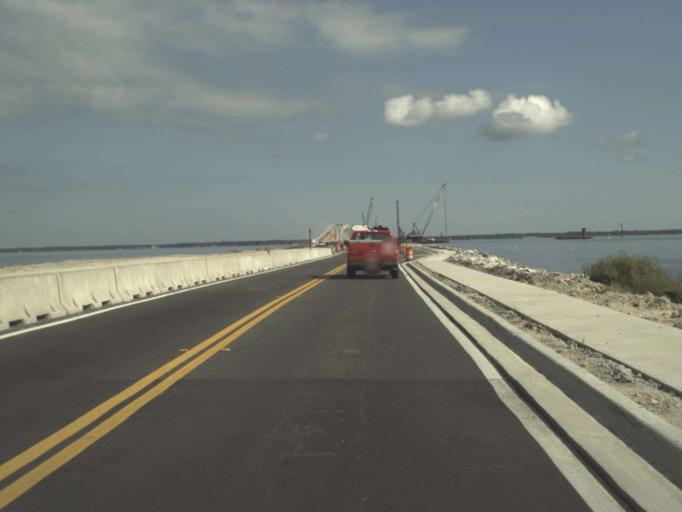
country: US
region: Florida
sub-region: Walton County
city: Seaside
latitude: 30.3901
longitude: -86.1732
